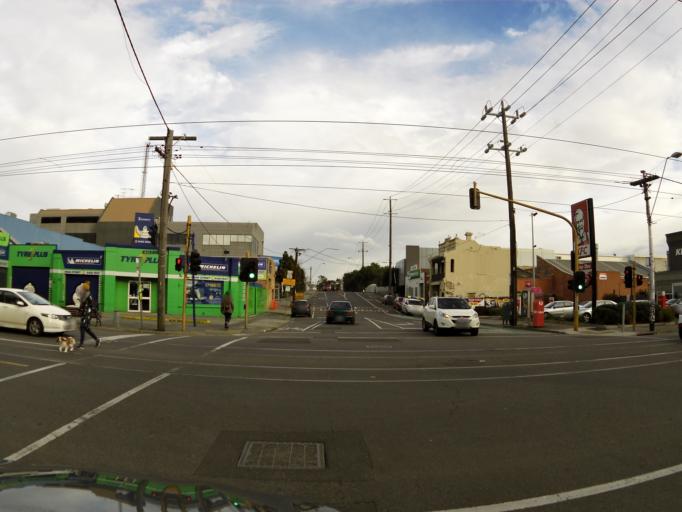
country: AU
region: Victoria
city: Albert Park
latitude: -37.8261
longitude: 145.0025
